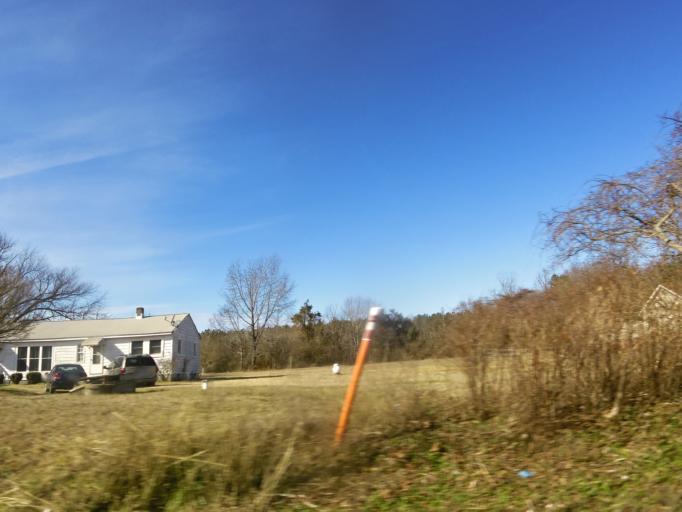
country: US
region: Virginia
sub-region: Isle of Wight County
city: Isle of Wight
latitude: 36.9499
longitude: -76.6787
